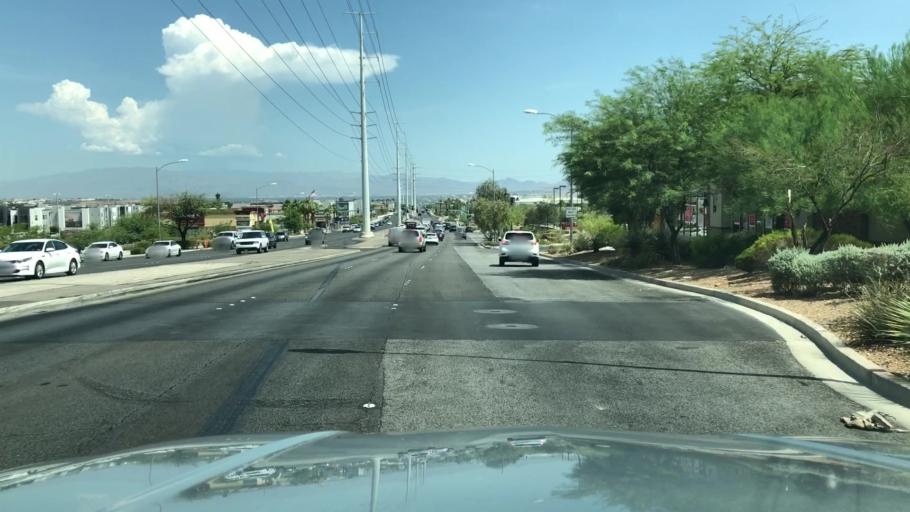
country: US
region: Nevada
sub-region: Clark County
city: Whitney
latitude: 36.0320
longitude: -115.0470
